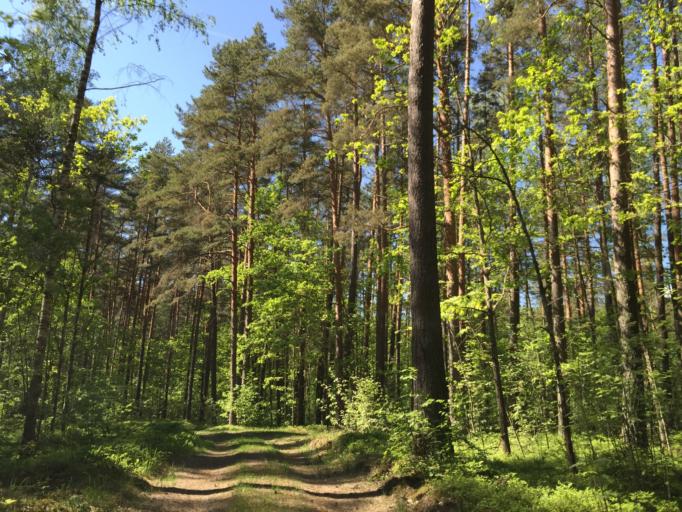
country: LV
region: Bauskas Rajons
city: Bauska
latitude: 56.4238
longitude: 24.2993
